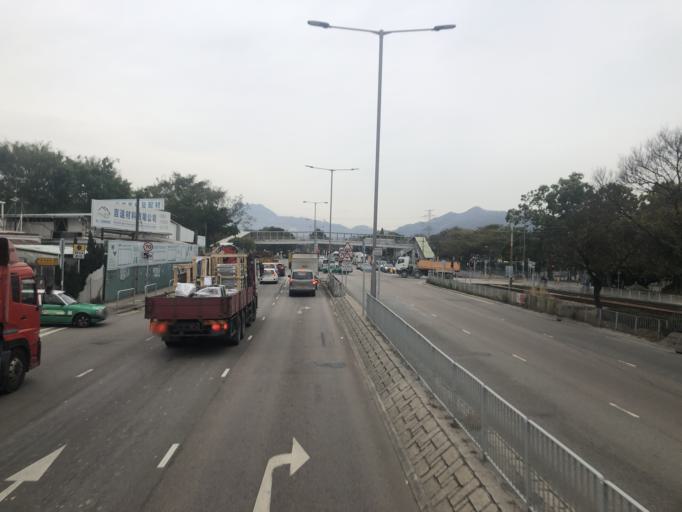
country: HK
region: Yuen Long
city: Yuen Long Kau Hui
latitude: 22.4309
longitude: 113.9939
